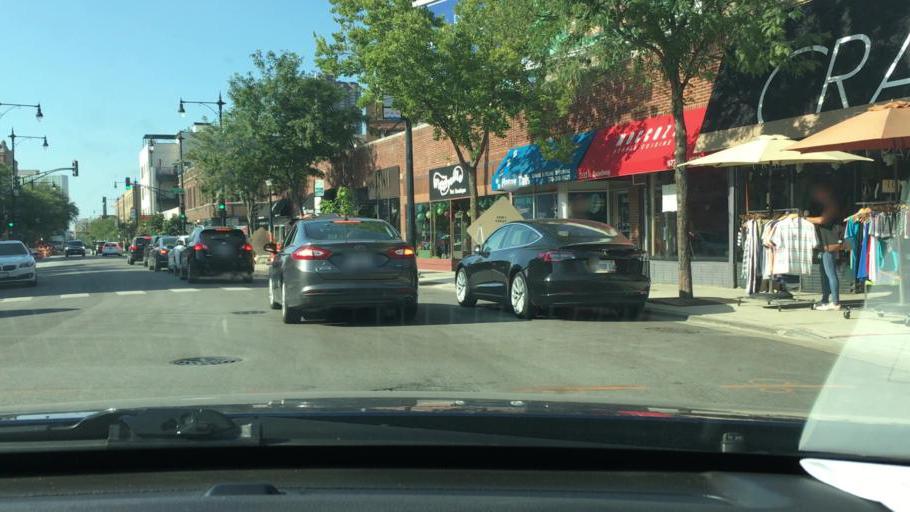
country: US
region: Illinois
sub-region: Cook County
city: Chicago
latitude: 41.9427
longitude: -87.6446
